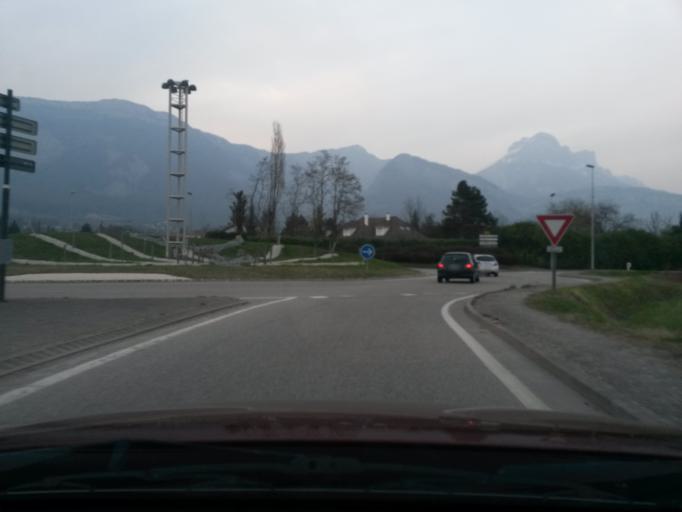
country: FR
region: Rhone-Alpes
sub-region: Departement de l'Isere
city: Saint-Nazaire-les-Eymes
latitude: 45.2404
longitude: 5.8469
